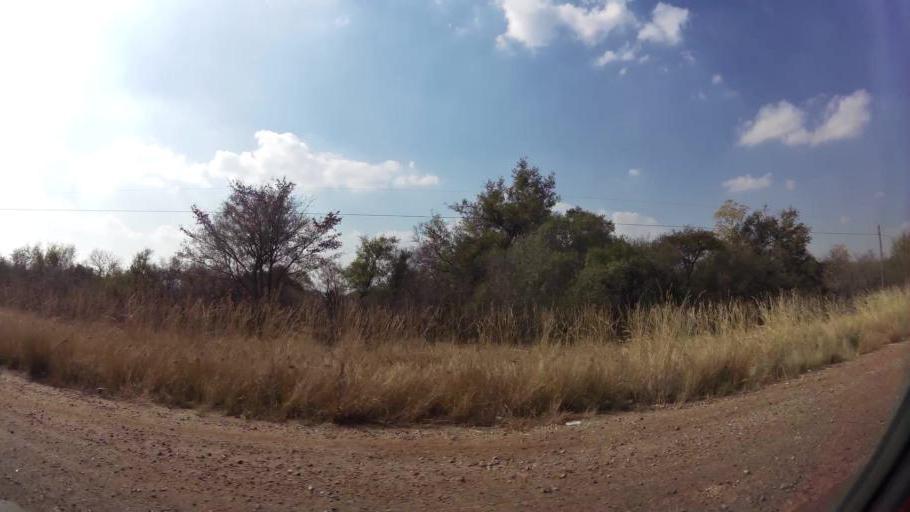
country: ZA
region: North-West
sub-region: Bojanala Platinum District Municipality
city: Rustenburg
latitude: -25.5223
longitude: 27.1072
